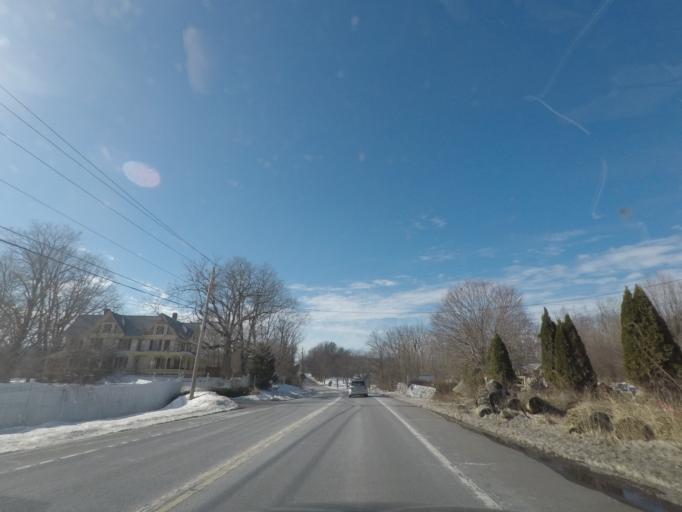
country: US
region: New York
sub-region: Schenectady County
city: Rotterdam
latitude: 42.7356
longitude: -73.9877
